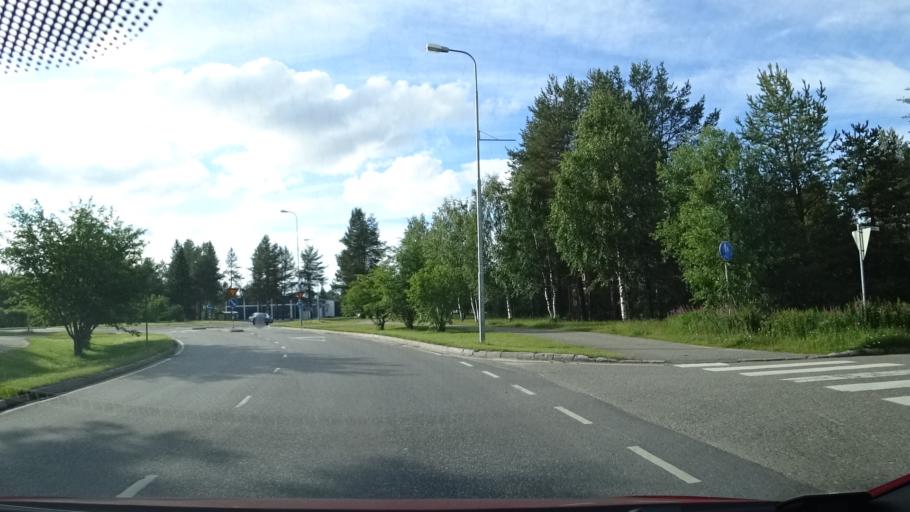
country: FI
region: Lapland
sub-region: Pohjois-Lappi
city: Sodankylae
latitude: 67.4209
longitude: 26.5896
